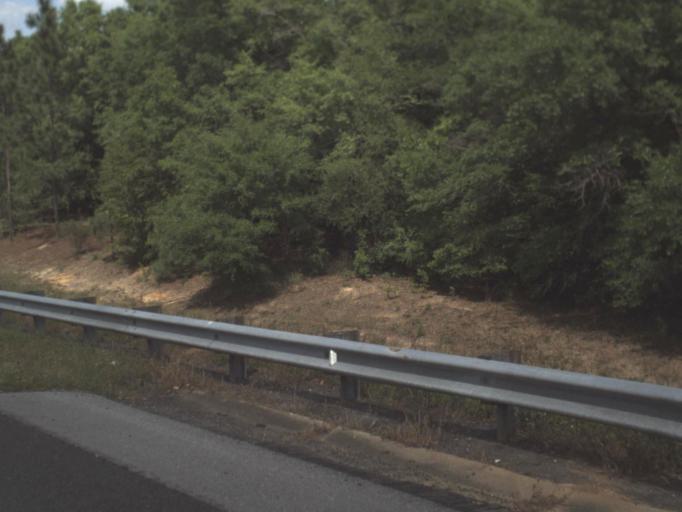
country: US
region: Florida
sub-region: Escambia County
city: Century
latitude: 30.8953
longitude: -87.3206
